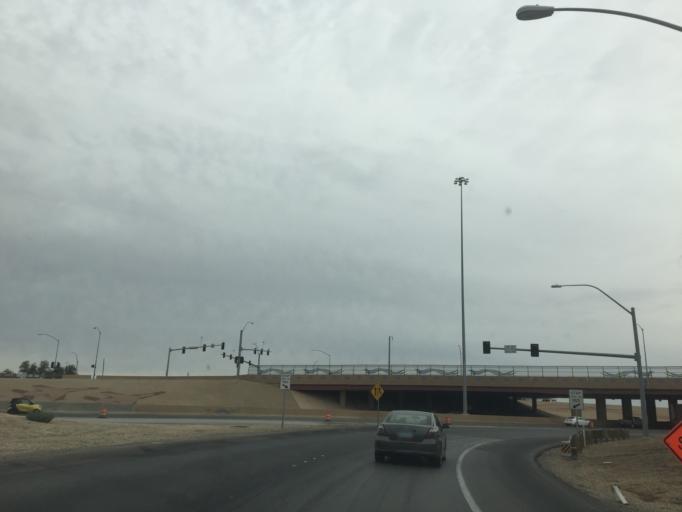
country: US
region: Nevada
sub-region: Clark County
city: Sunrise Manor
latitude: 36.2415
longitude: -115.1017
